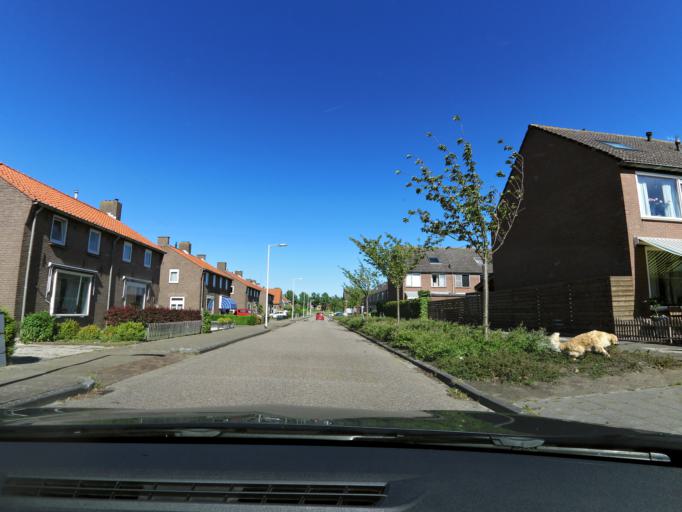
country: NL
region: South Holland
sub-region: Gemeente Hellevoetsluis
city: Hellevoetsluis
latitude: 51.8391
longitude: 4.1419
